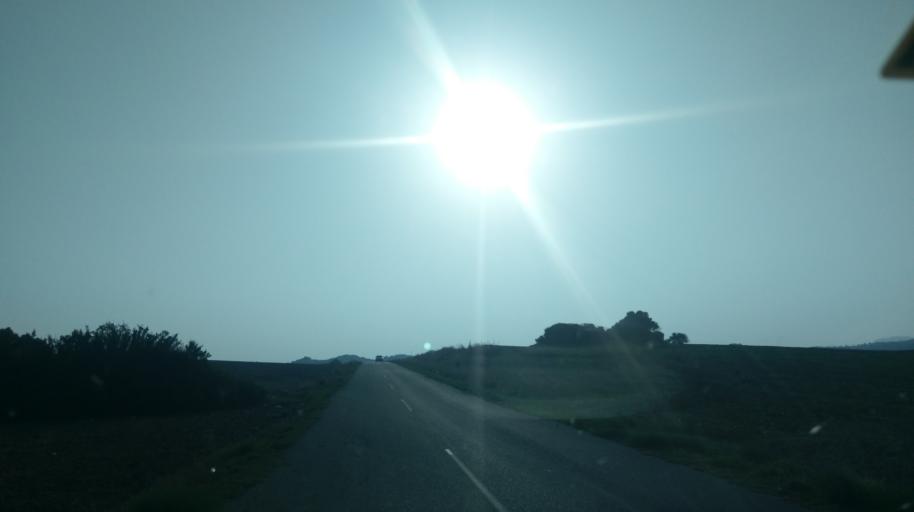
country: CY
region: Ammochostos
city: Leonarisso
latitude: 35.4649
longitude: 34.0999
